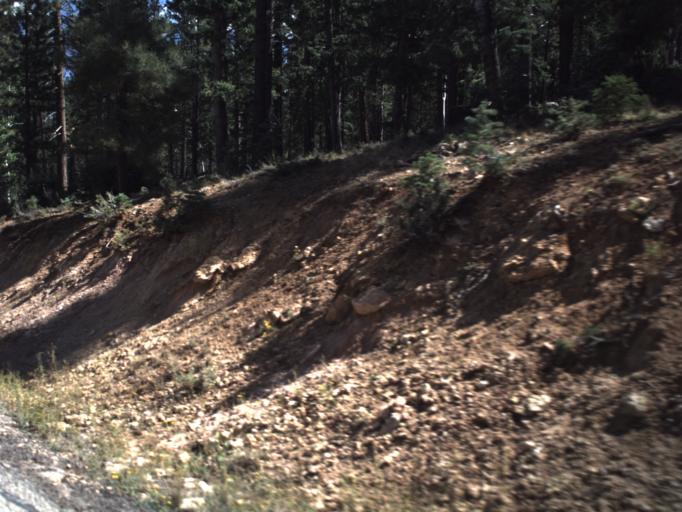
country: US
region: Utah
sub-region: Garfield County
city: Panguitch
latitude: 37.5139
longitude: -112.6370
